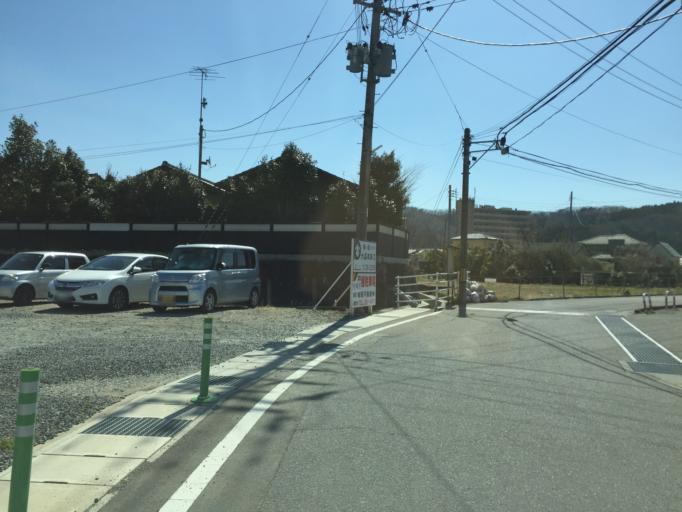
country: JP
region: Fukushima
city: Iwaki
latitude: 37.0379
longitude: 140.8534
